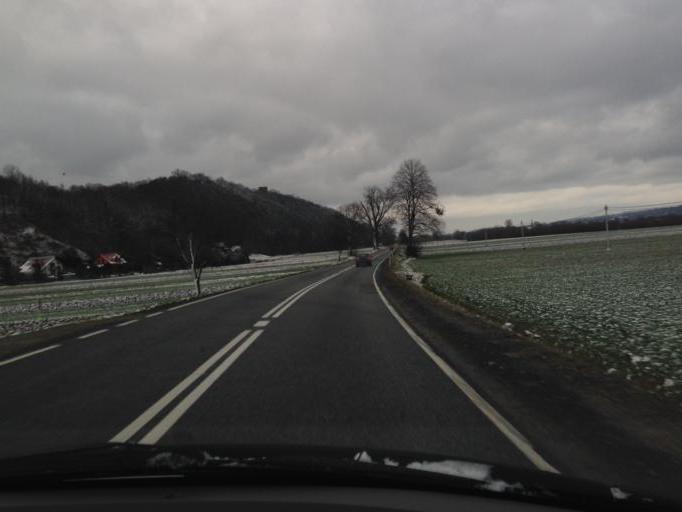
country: PL
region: Lesser Poland Voivodeship
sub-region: Powiat tarnowski
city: Zakliczyn
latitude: 49.8686
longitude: 20.7571
